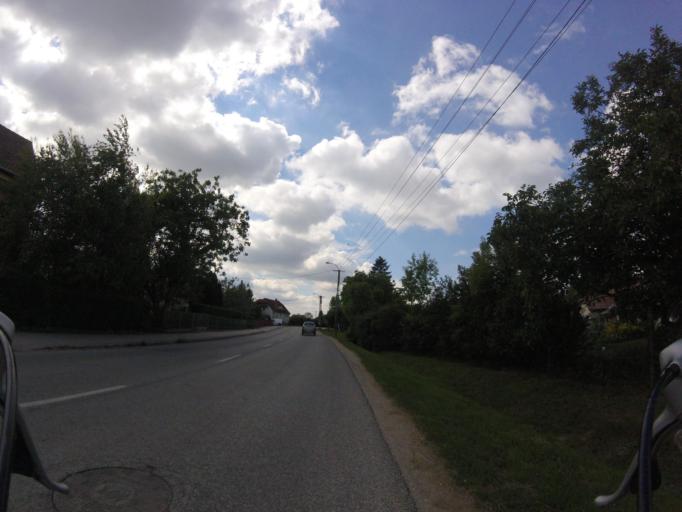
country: HU
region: Fejer
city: Szabadbattyan
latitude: 47.0813
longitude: 18.4095
